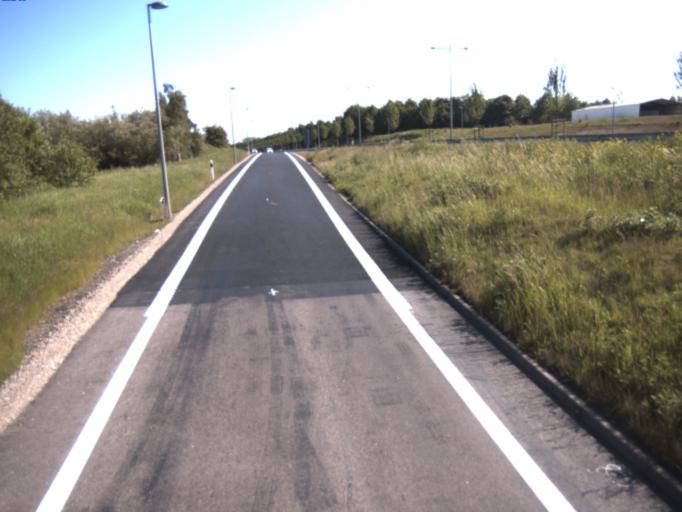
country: SE
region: Skane
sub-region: Helsingborg
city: Odakra
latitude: 56.0727
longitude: 12.7406
